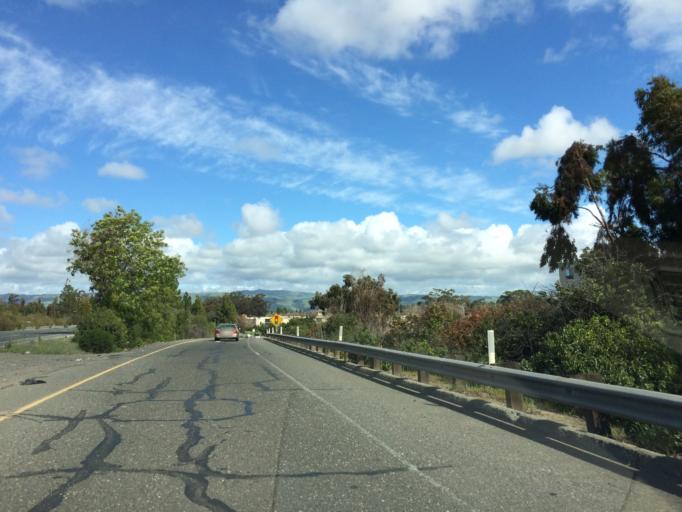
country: US
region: California
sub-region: Alameda County
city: Newark
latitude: 37.5503
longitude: -122.0539
